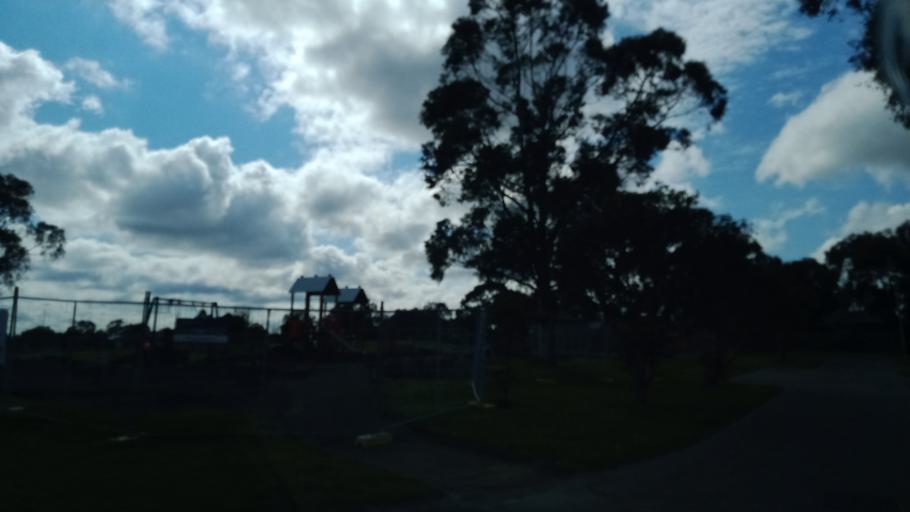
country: AU
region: Victoria
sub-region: Frankston
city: Carrum Downs
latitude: -38.0889
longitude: 145.1855
